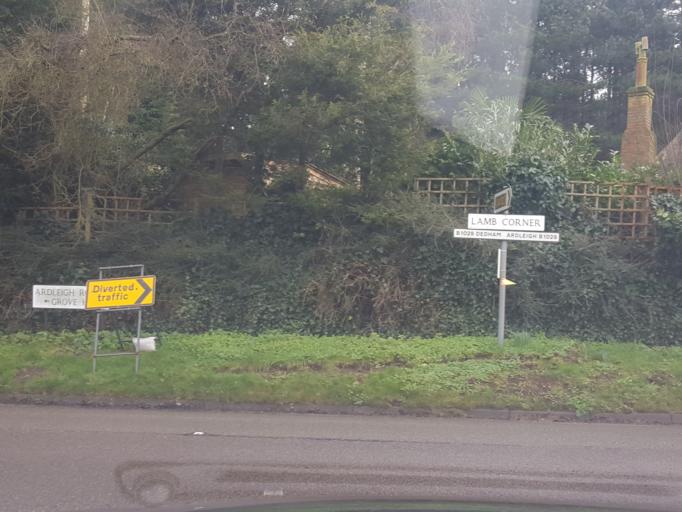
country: GB
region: England
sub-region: Suffolk
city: East Bergholt
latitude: 51.9453
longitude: 0.9755
